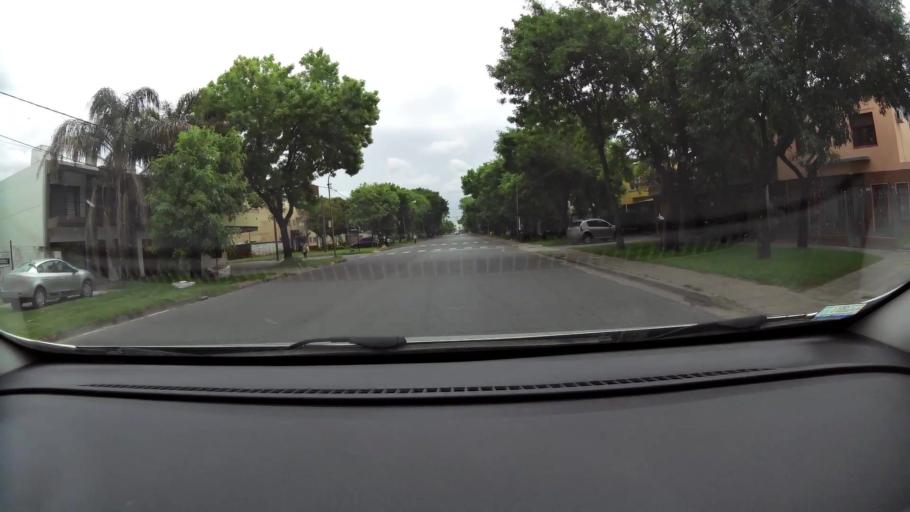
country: AR
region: Buenos Aires
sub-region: Partido de Campana
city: Campana
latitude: -34.1625
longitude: -58.9721
